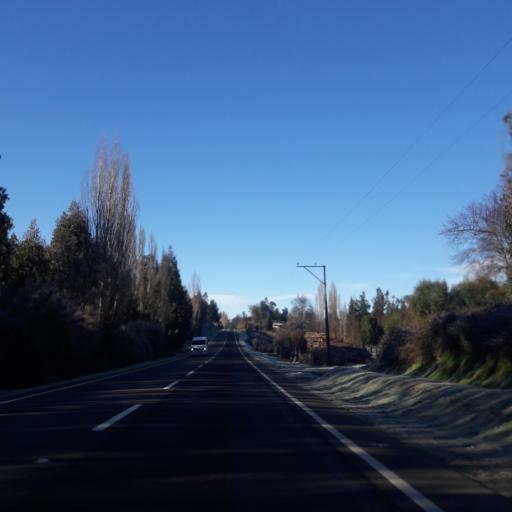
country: CL
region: Biobio
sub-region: Provincia de Biobio
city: La Laja
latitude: -37.3197
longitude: -72.9203
